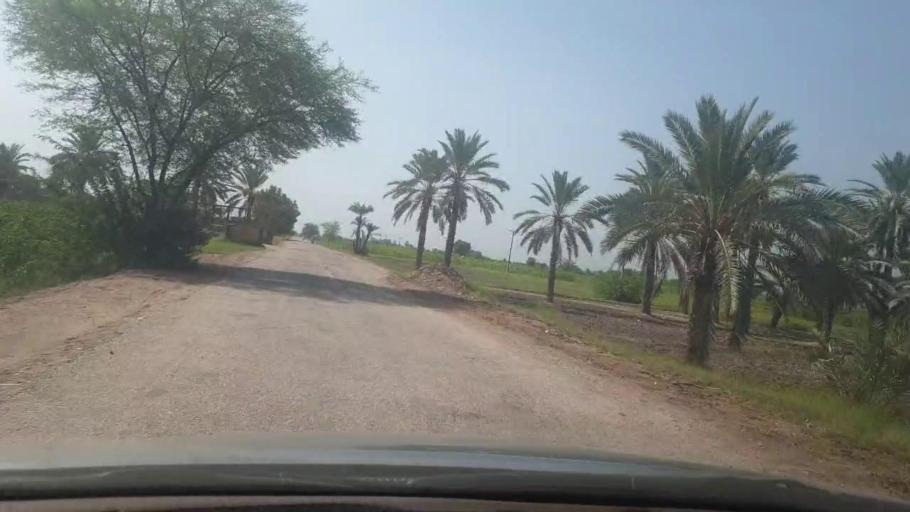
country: PK
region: Sindh
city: Gambat
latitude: 27.3151
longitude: 68.5595
